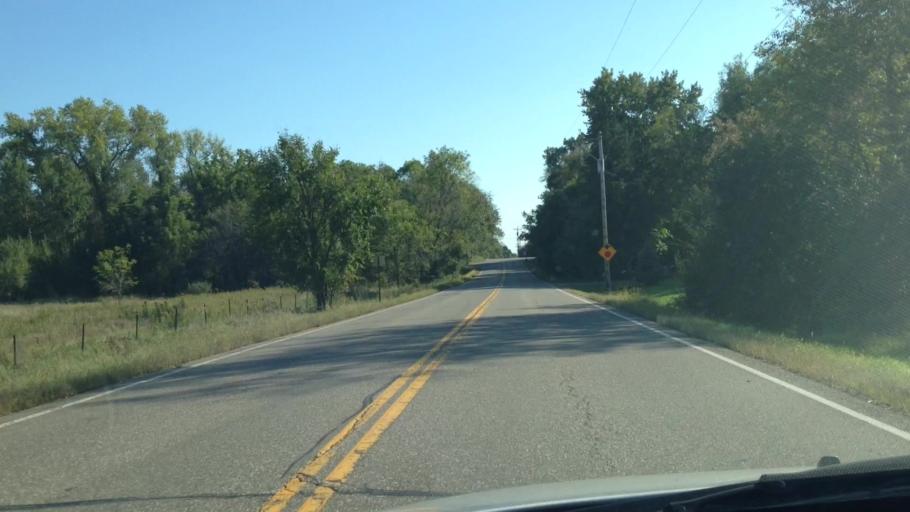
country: US
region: Minnesota
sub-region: Washington County
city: Stillwater
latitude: 45.1022
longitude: -92.8129
